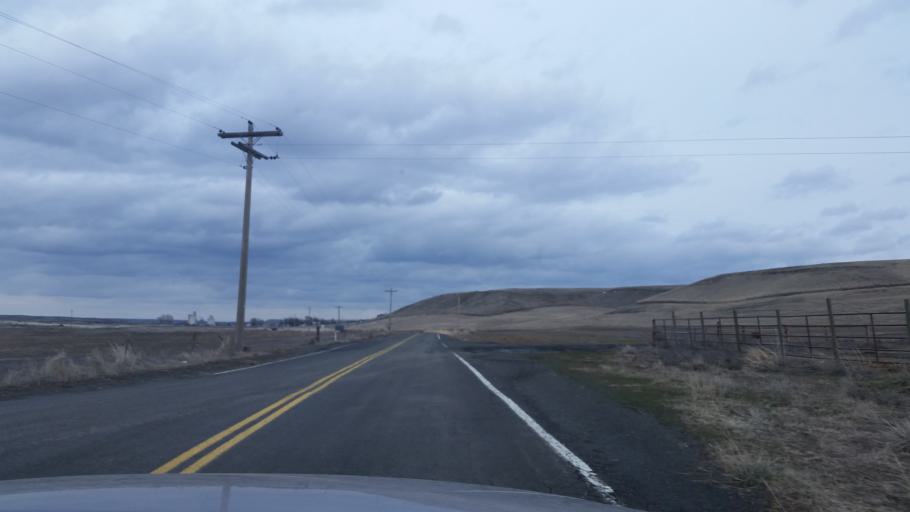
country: US
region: Washington
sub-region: Adams County
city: Ritzville
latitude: 47.1845
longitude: -117.9287
